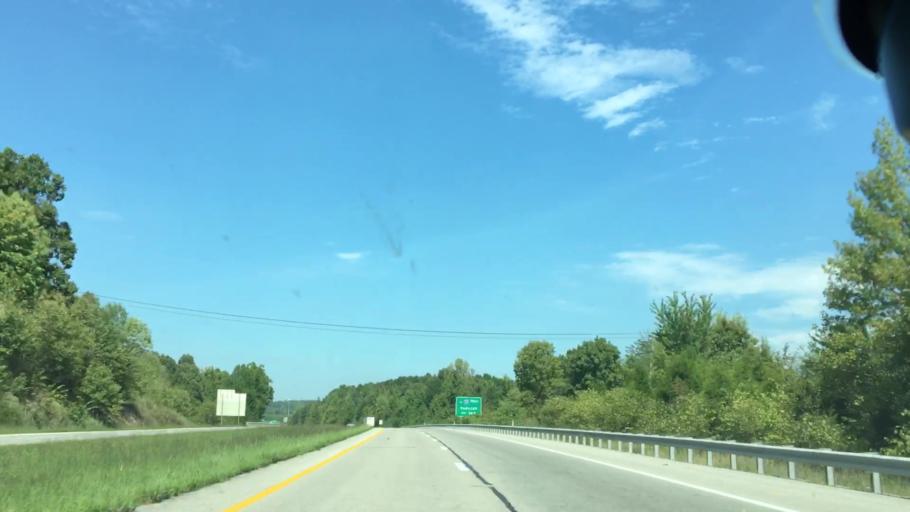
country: US
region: Kentucky
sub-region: Hopkins County
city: Nortonville
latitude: 37.2002
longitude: -87.4395
